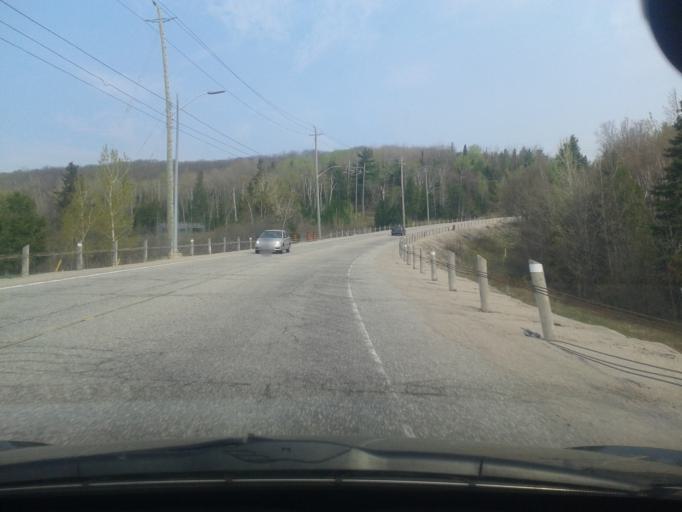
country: CA
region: Ontario
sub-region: Nipissing District
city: North Bay
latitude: 46.3353
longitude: -79.4935
